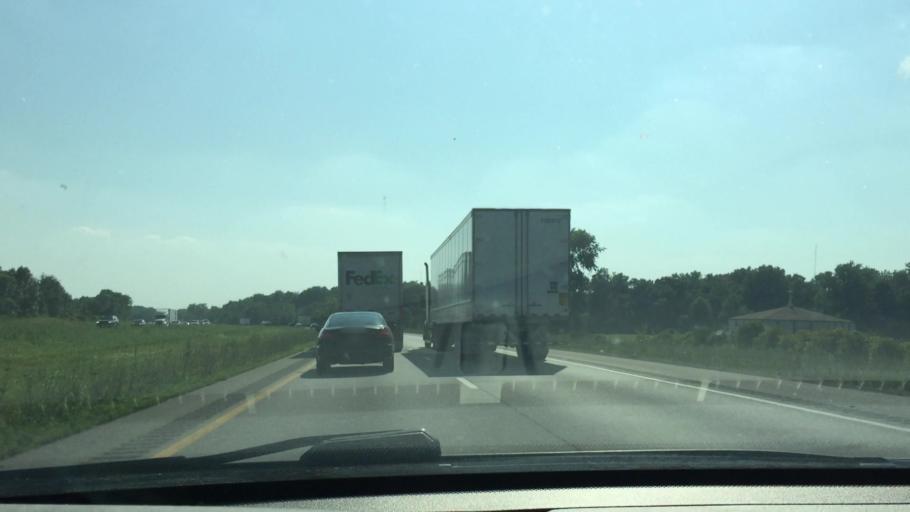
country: US
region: Ohio
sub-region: Franklin County
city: Reynoldsburg
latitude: 39.9511
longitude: -82.7472
